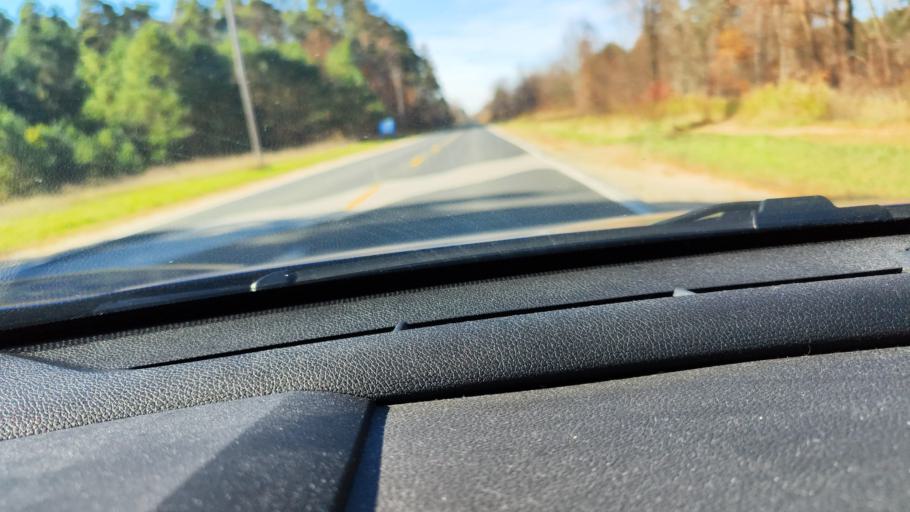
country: CA
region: Ontario
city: Angus
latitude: 44.3548
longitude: -79.9878
